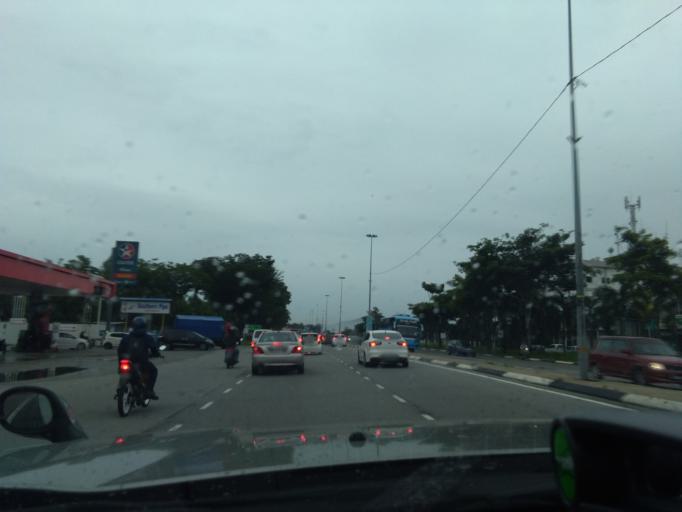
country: MY
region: Penang
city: Nibong Tebal
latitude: 5.1752
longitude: 100.4811
